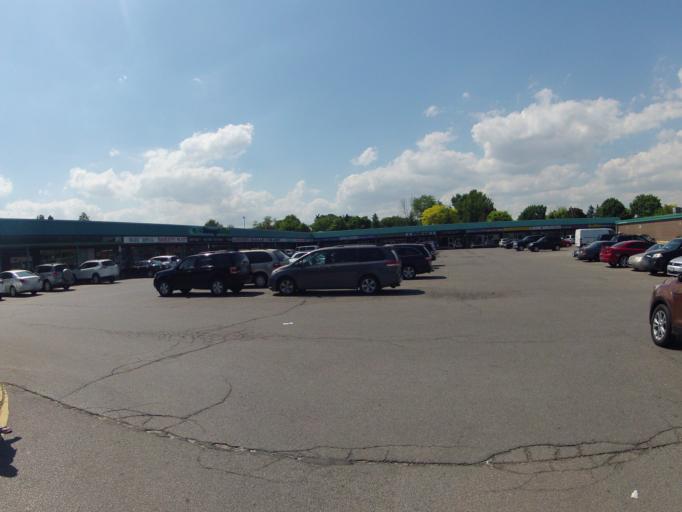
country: CA
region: Ontario
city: Mississauga
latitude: 43.5123
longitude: -79.6489
